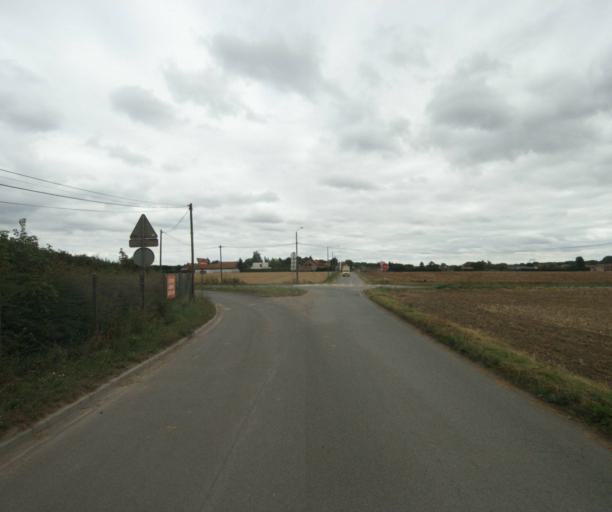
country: FR
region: Nord-Pas-de-Calais
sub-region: Departement du Nord
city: Fretin
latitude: 50.5629
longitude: 3.1395
